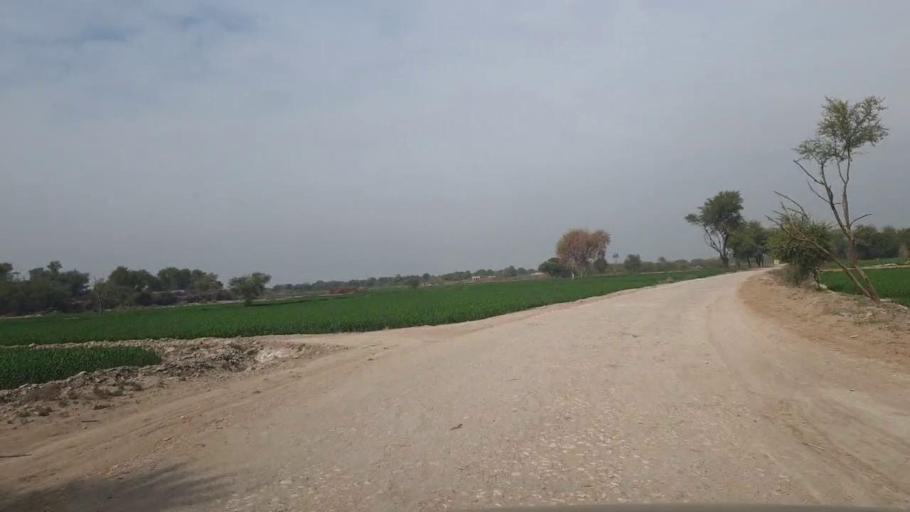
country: PK
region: Sindh
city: Nawabshah
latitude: 26.1130
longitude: 68.4801
